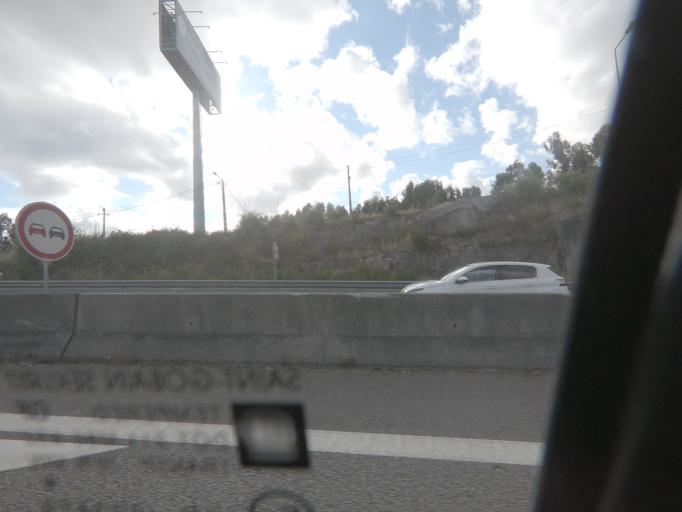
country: PT
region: Porto
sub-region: Maia
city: Pedroucos
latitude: 41.1944
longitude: -8.5914
